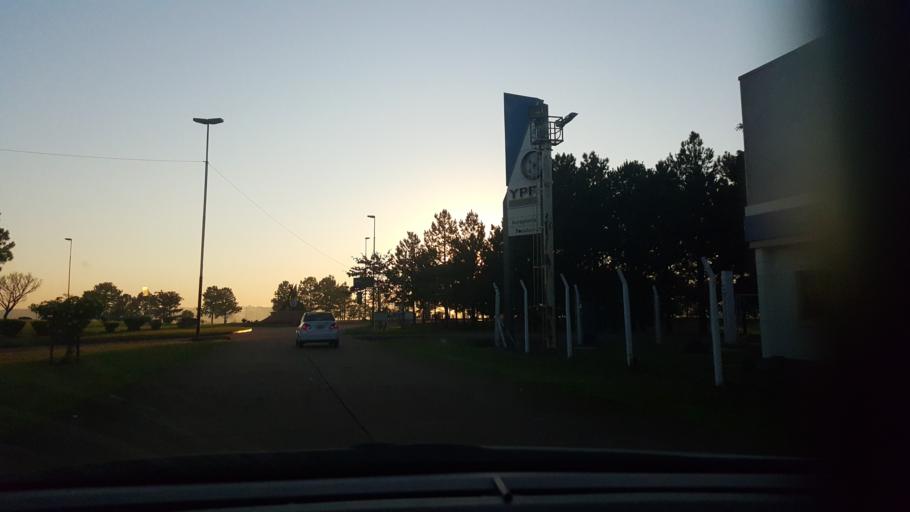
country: AR
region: Misiones
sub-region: Departamento de Capital
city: Posadas
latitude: -27.3924
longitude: -55.9658
